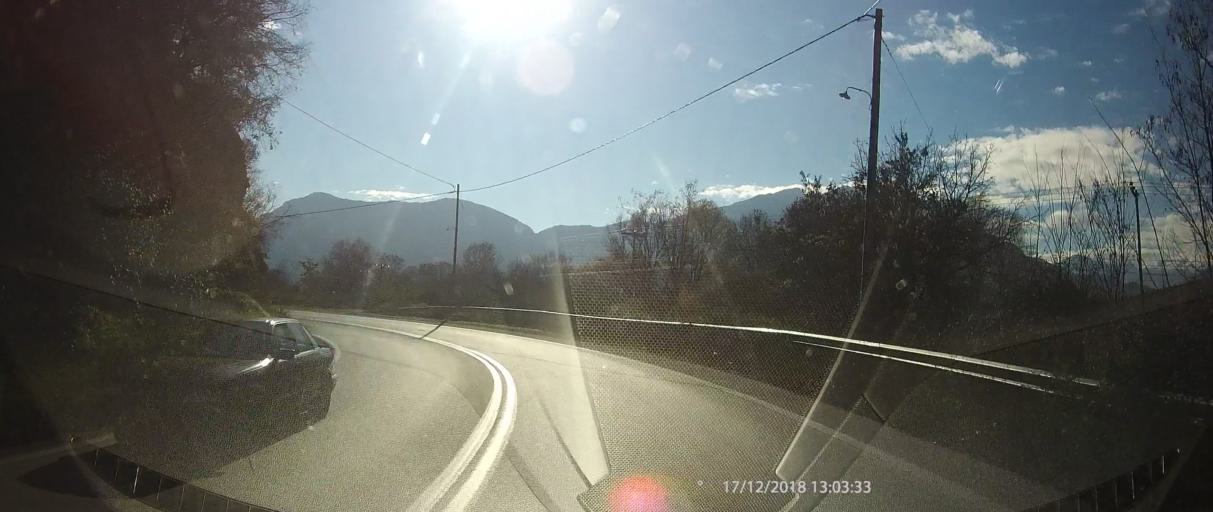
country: GR
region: Thessaly
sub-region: Trikala
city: Kastraki
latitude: 39.7112
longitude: 21.6009
